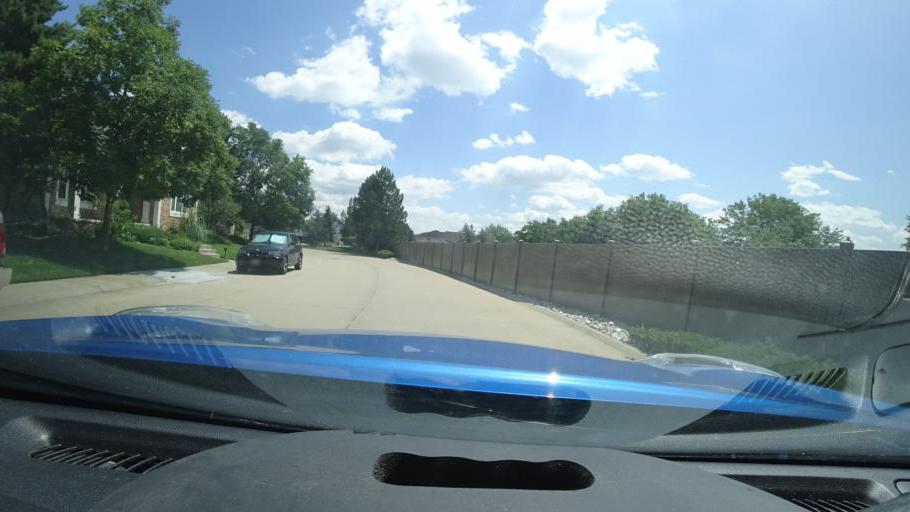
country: US
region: Colorado
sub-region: Arapahoe County
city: Glendale
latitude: 39.6985
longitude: -104.8958
